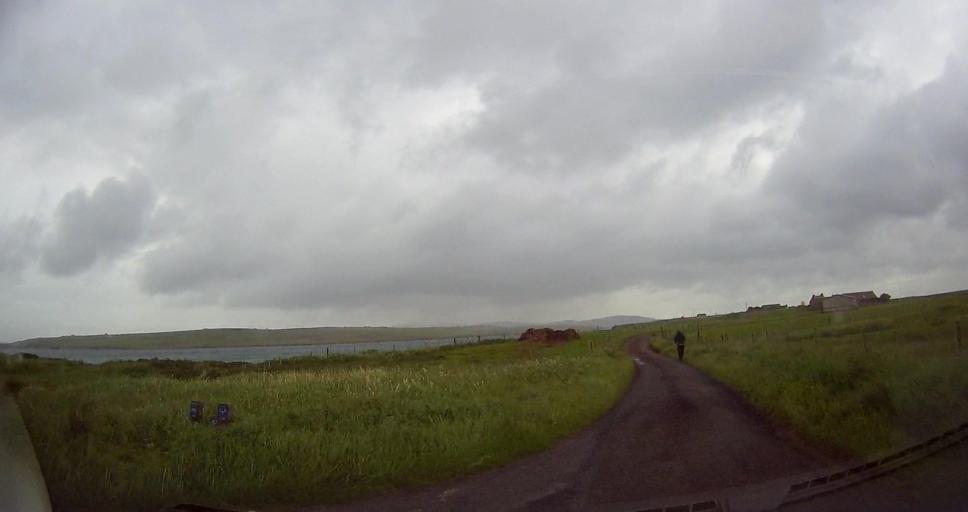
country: GB
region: Scotland
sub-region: Orkney Islands
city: Stromness
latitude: 58.9164
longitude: -3.3238
